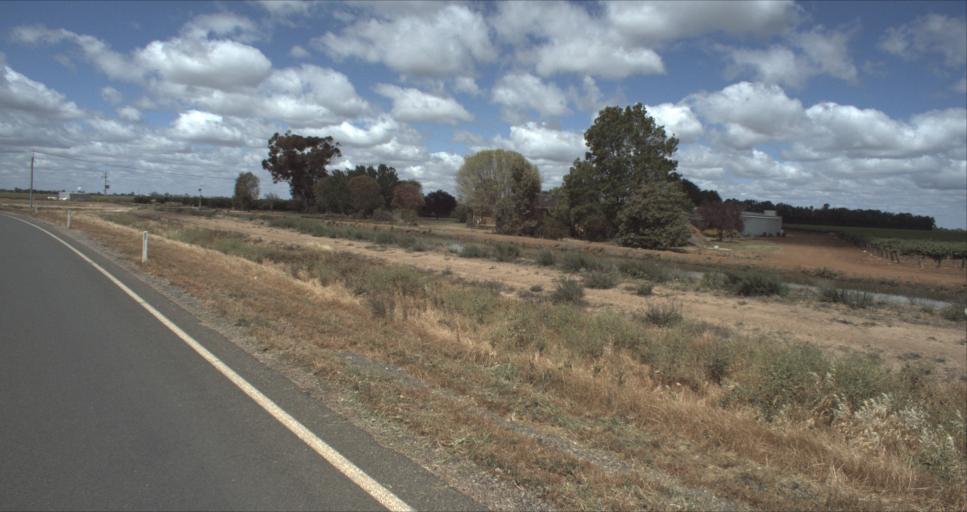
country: AU
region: New South Wales
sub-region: Murrumbidgee Shire
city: Darlington Point
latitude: -34.4935
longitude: 146.1673
